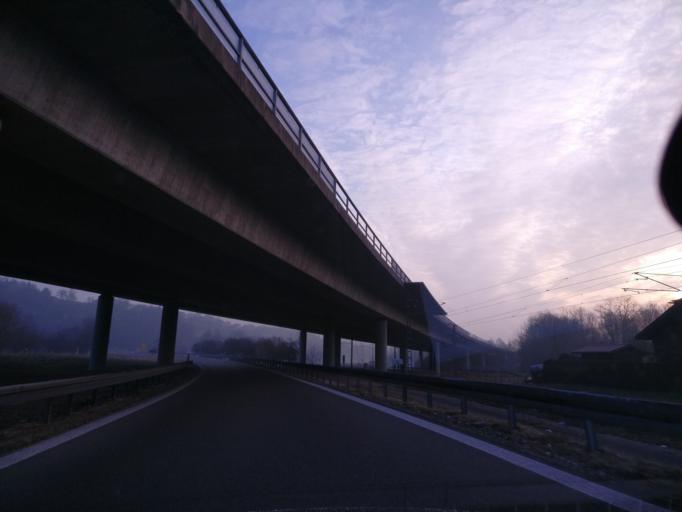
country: DE
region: Baden-Wuerttemberg
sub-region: Regierungsbezirk Stuttgart
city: Lorch
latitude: 48.7972
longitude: 9.6620
